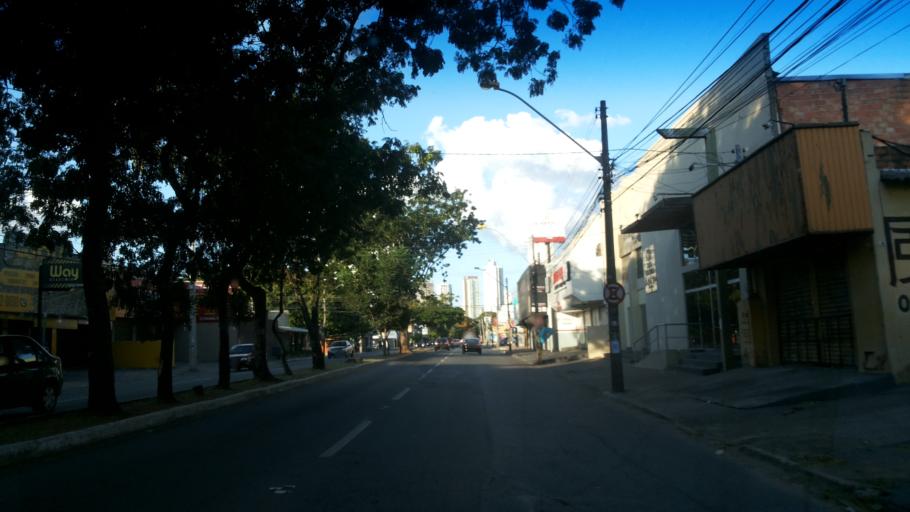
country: BR
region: Goias
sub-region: Goiania
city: Goiania
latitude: -16.7085
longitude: -49.2860
